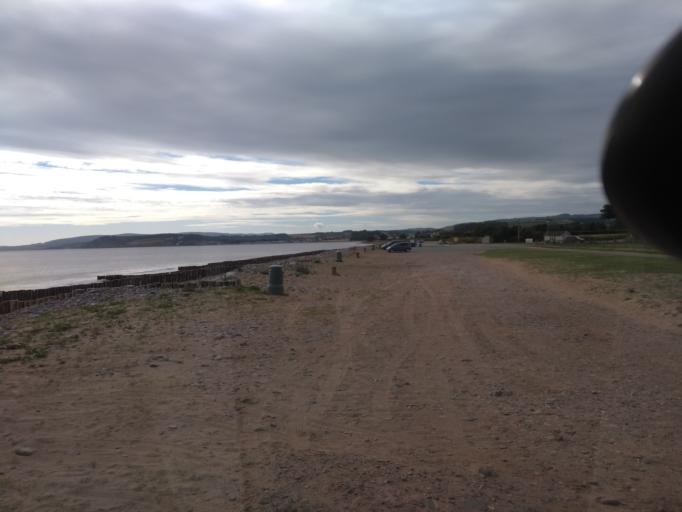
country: GB
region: England
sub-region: Somerset
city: Minehead
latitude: 51.1922
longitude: -3.4271
